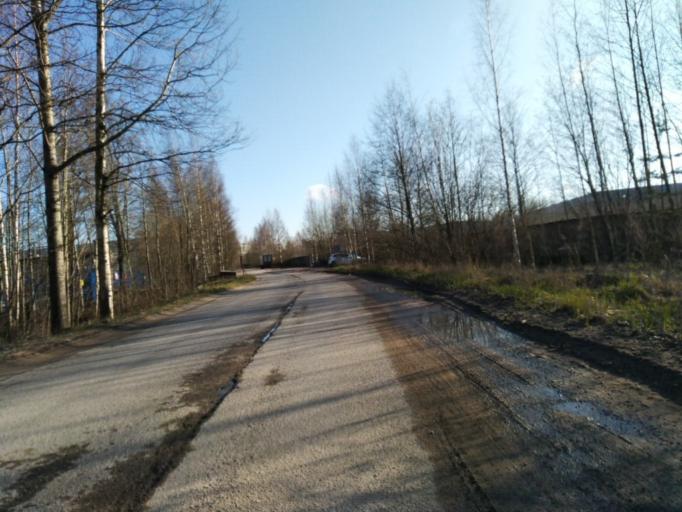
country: RU
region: Leningrad
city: Novoye Devyatkino
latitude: 60.0702
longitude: 30.4806
